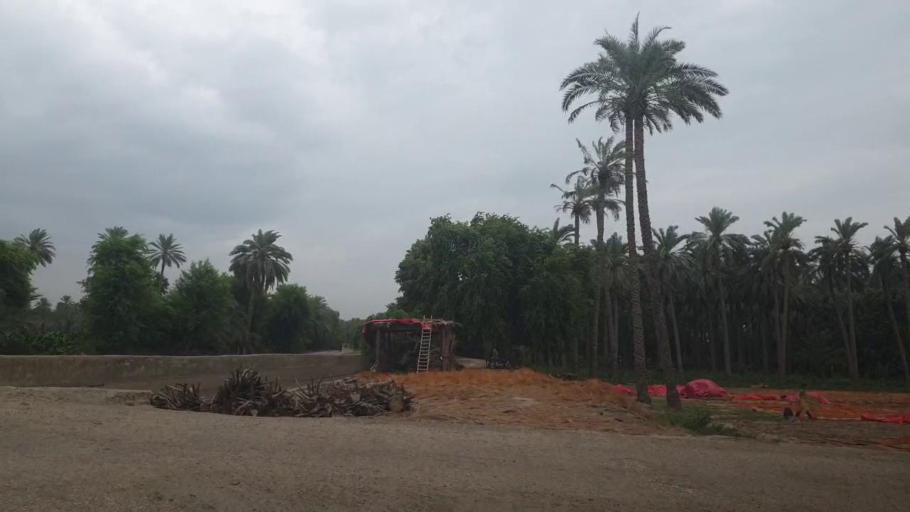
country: PK
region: Sindh
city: Khairpur
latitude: 27.5975
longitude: 68.7559
